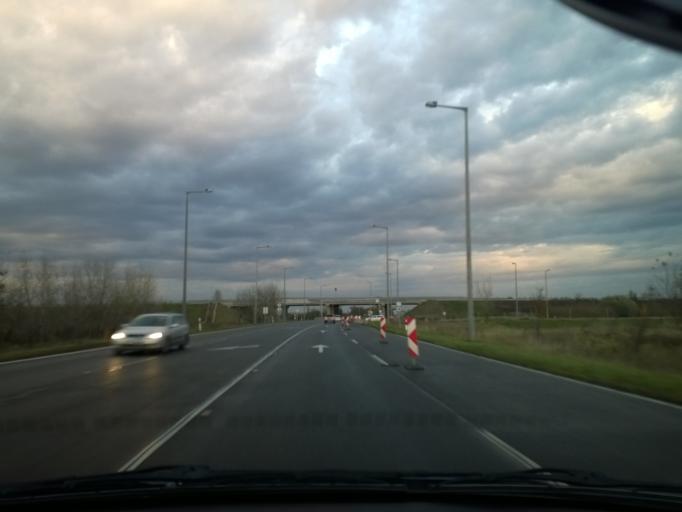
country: HU
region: Bacs-Kiskun
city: Dunavecse
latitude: 46.8949
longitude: 18.9835
